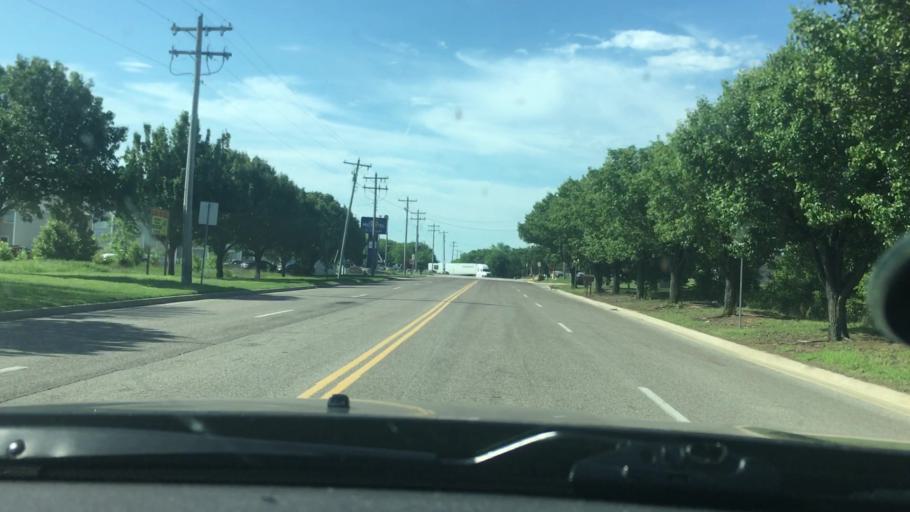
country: US
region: Oklahoma
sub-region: Carter County
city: Ardmore
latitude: 34.1897
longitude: -97.1703
